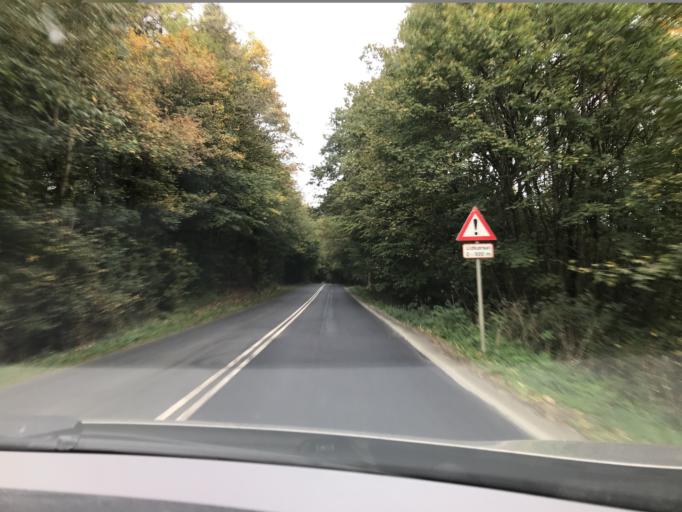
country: DK
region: South Denmark
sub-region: Kolding Kommune
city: Kolding
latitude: 55.5321
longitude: 9.4206
